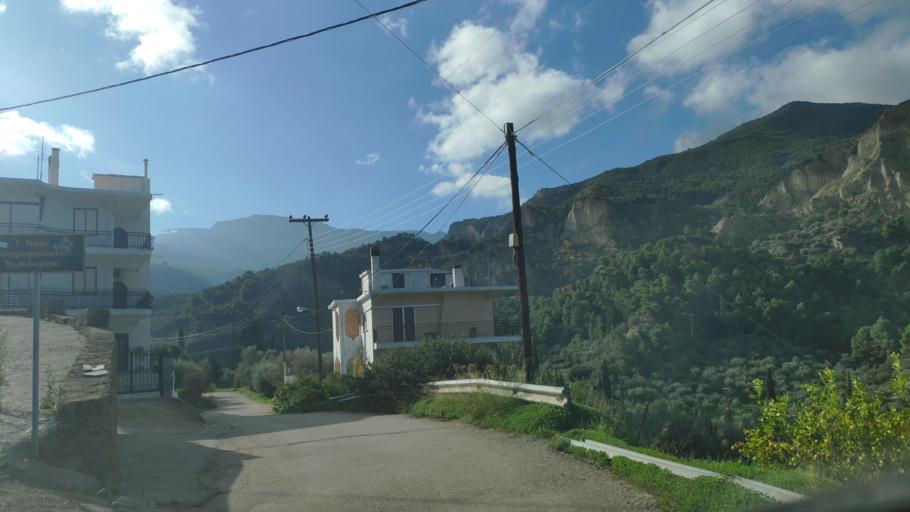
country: GR
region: West Greece
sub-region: Nomos Achaias
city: Aiyira
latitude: 38.1210
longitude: 22.4355
